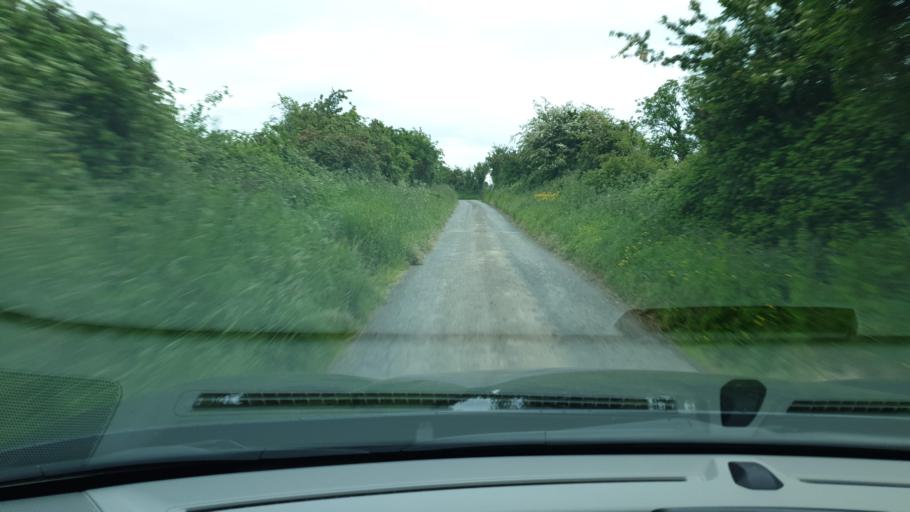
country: IE
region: Leinster
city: Balrothery
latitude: 53.5598
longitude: -6.1973
